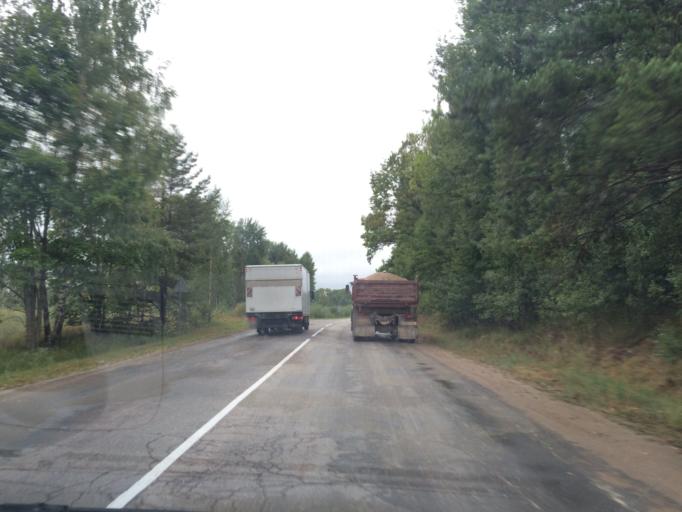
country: LV
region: Ikskile
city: Ikskile
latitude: 56.8551
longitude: 24.5316
